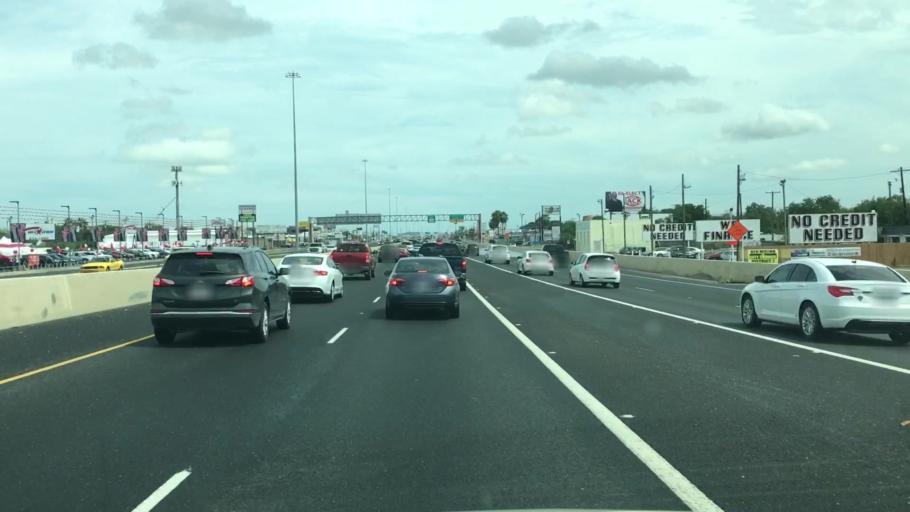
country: US
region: Texas
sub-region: Nueces County
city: Corpus Christi
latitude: 27.7347
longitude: -97.4257
